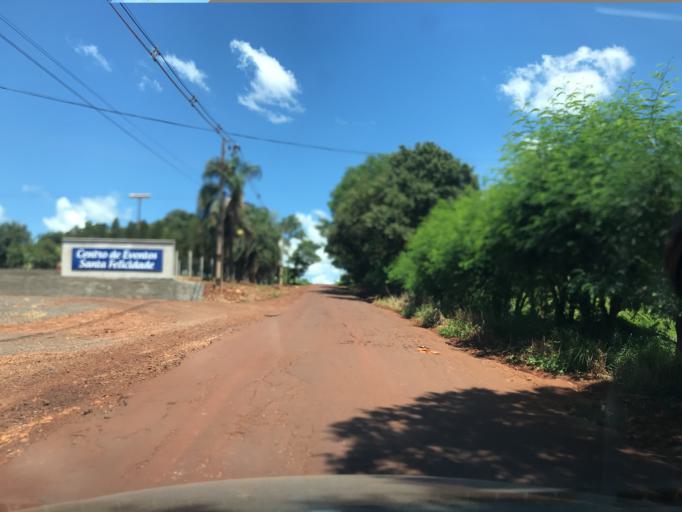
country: BR
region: Parana
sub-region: Palotina
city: Palotina
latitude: -24.2938
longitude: -53.8541
